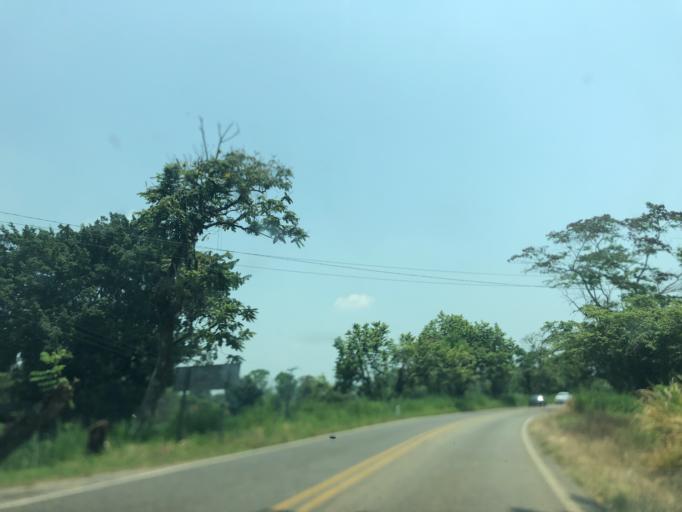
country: MX
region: Tabasco
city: Teapa
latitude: 17.5662
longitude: -92.9718
